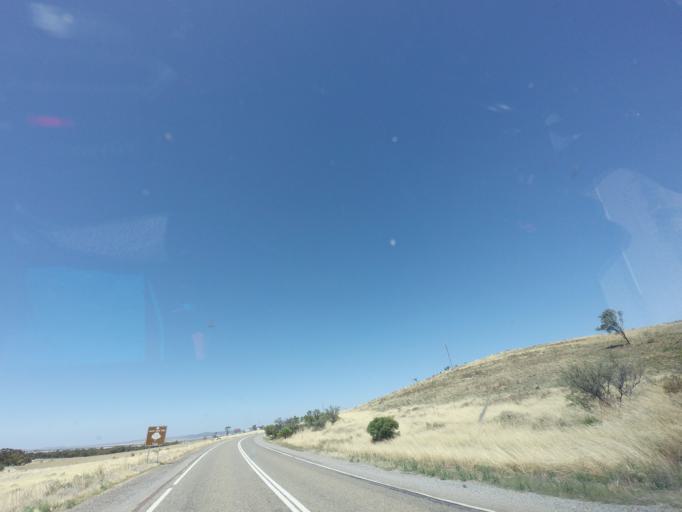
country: AU
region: South Australia
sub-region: Peterborough
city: Peterborough
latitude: -32.7322
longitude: 138.5946
